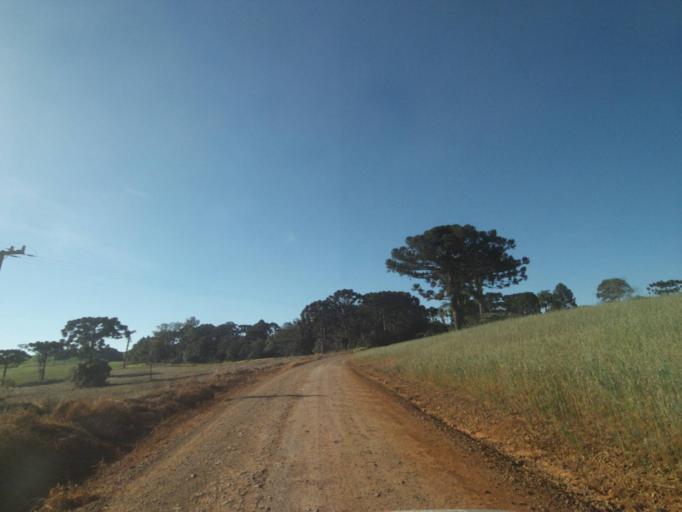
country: BR
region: Parana
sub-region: Tibagi
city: Tibagi
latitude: -24.5365
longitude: -50.4967
